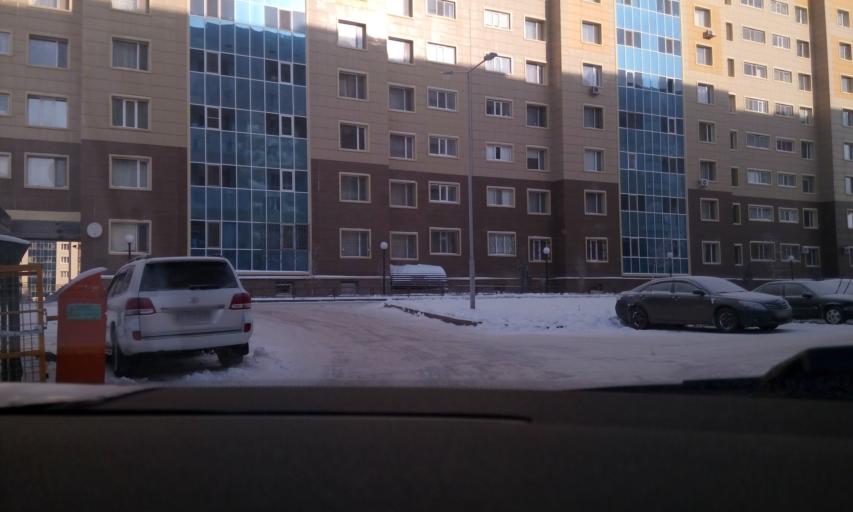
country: KZ
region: Astana Qalasy
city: Astana
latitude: 51.1216
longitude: 71.4184
